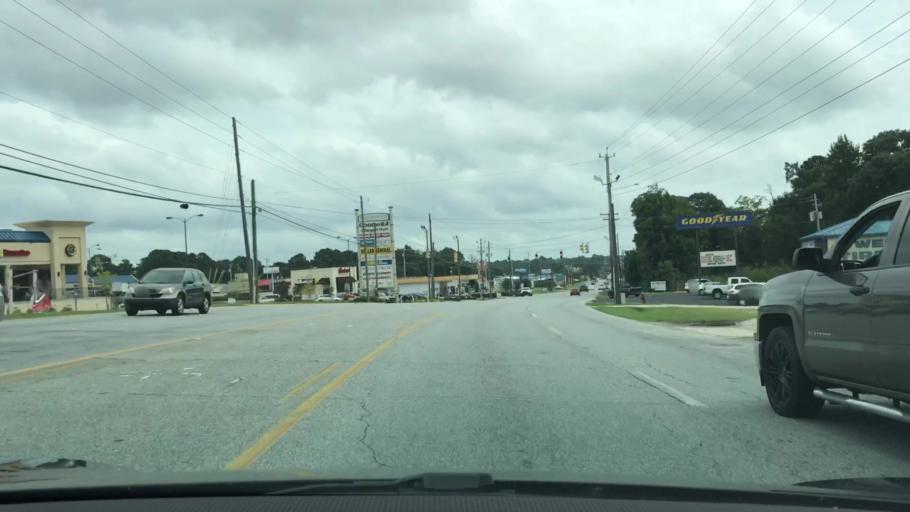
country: US
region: Alabama
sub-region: Lee County
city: Auburn
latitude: 32.6323
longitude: -85.4348
